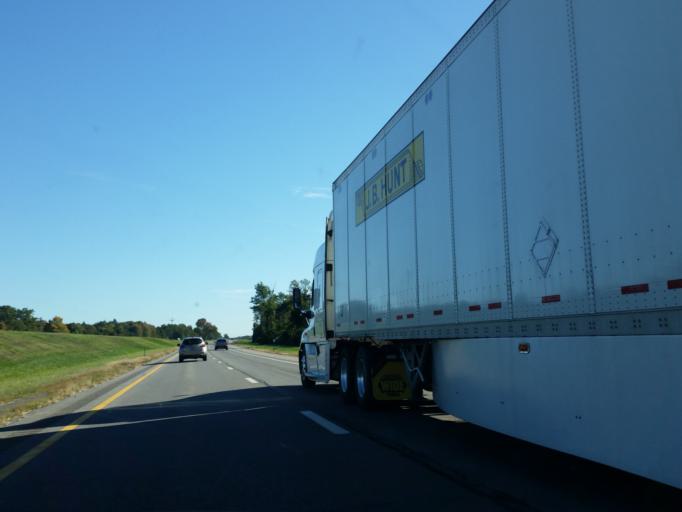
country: US
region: New York
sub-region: Erie County
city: Wanakah
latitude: 42.7273
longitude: -78.8773
